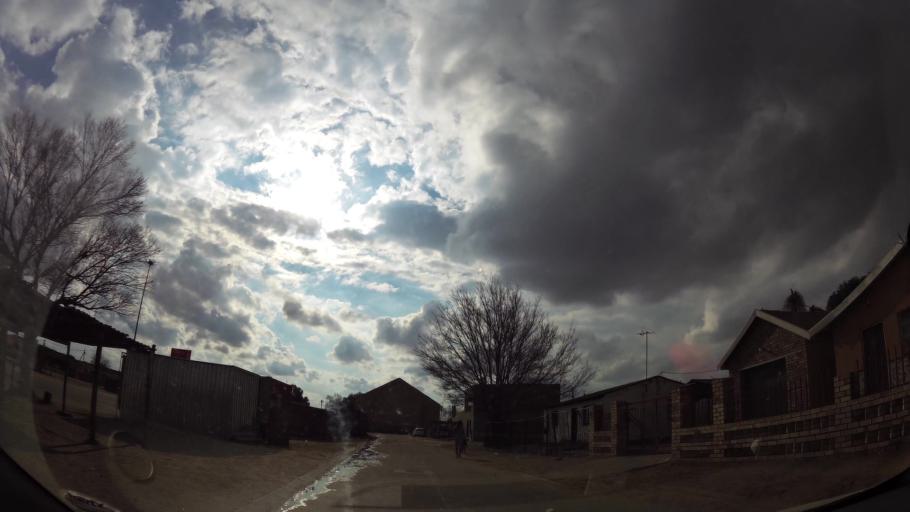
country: ZA
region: Orange Free State
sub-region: Fezile Dabi District Municipality
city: Sasolburg
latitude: -26.8401
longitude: 27.8455
